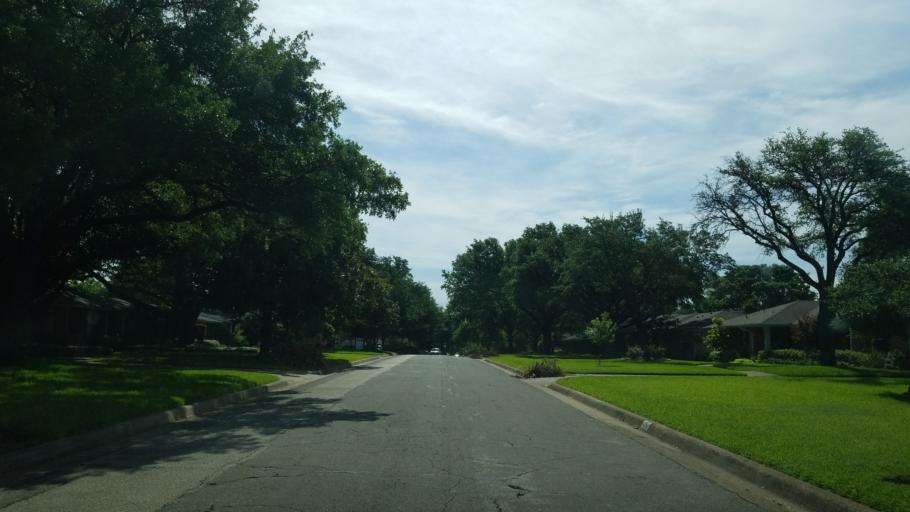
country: US
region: Texas
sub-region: Dallas County
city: Farmers Branch
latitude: 32.9043
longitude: -96.8532
